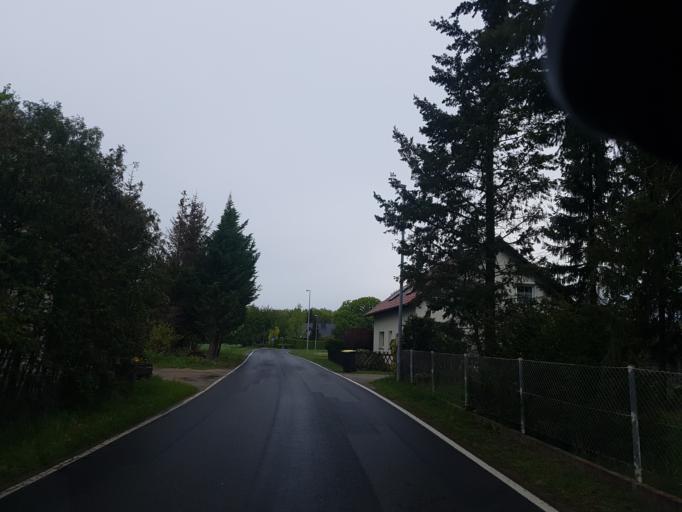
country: DE
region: Brandenburg
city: Spremberg
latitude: 51.6168
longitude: 14.4135
